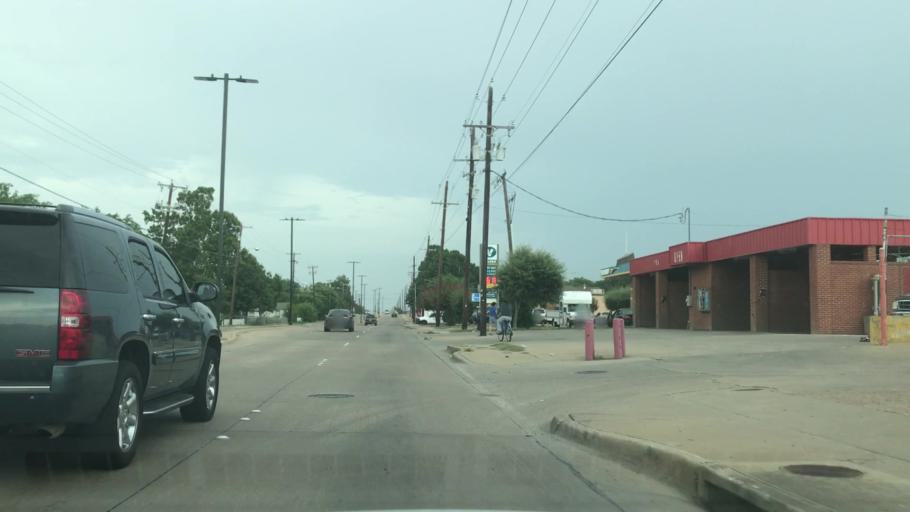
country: US
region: Texas
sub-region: Dallas County
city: Garland
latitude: 32.8788
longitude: -96.6549
